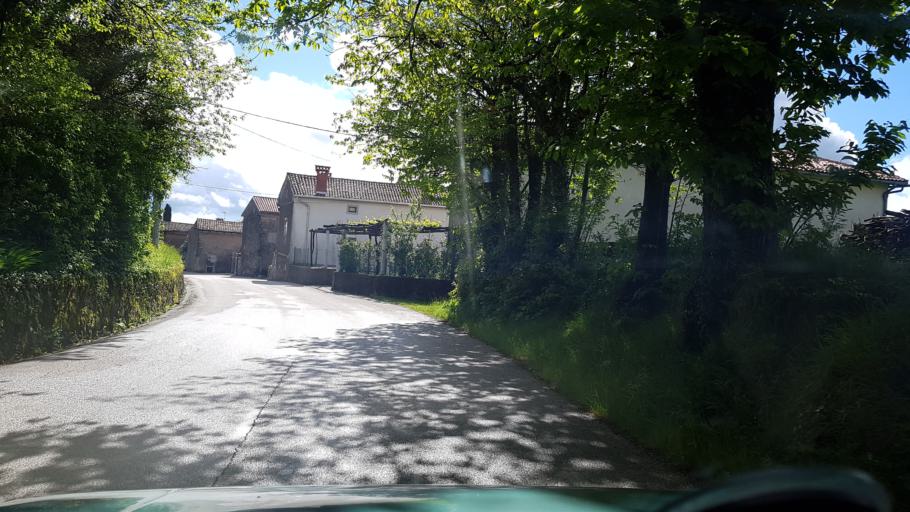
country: SI
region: Rence-Vogrsko
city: Rence
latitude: 45.8459
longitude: 13.6675
